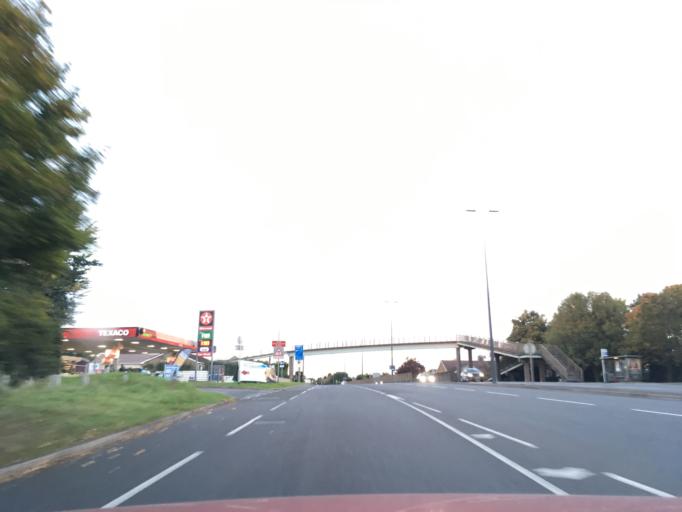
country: GB
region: England
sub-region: South Gloucestershire
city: Almondsbury
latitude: 51.5355
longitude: -2.5676
